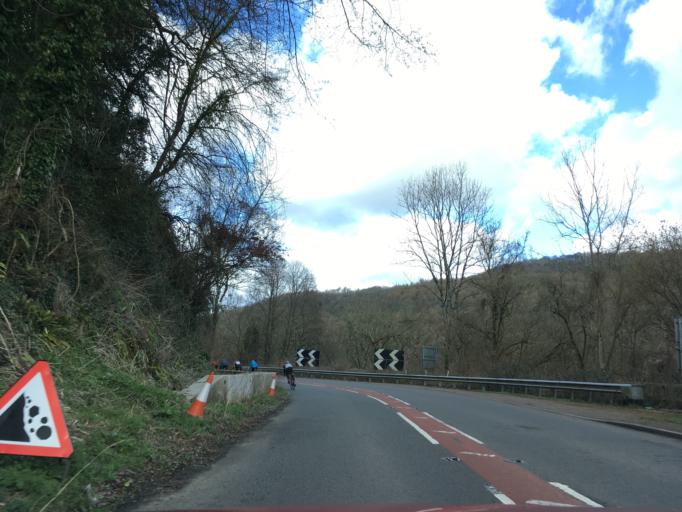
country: GB
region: Wales
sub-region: Monmouthshire
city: Tintern
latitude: 51.6915
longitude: -2.6713
